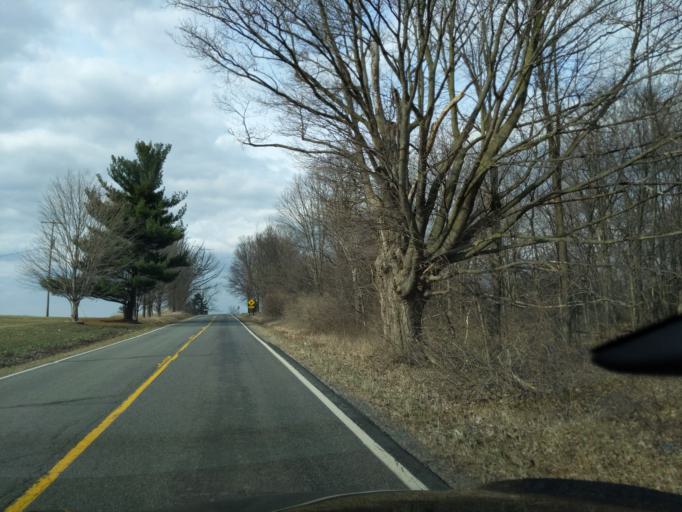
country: US
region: Michigan
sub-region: Ingham County
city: Mason
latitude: 42.5508
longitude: -84.4831
